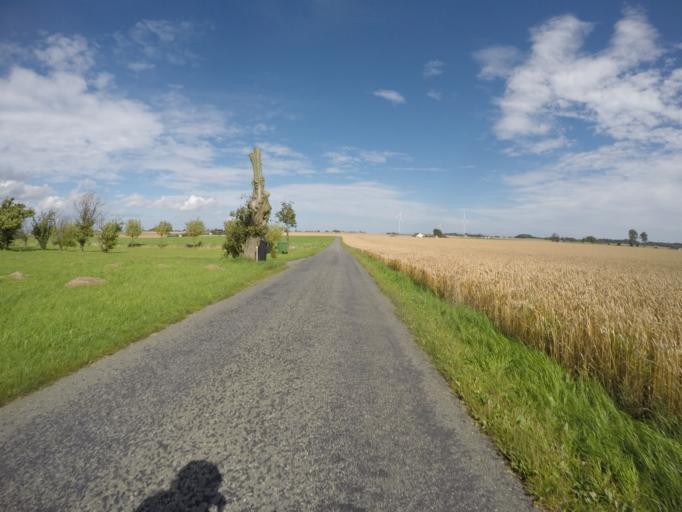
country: SE
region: Skane
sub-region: Tomelilla Kommun
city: Tomelilla
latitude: 55.4718
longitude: 14.1508
